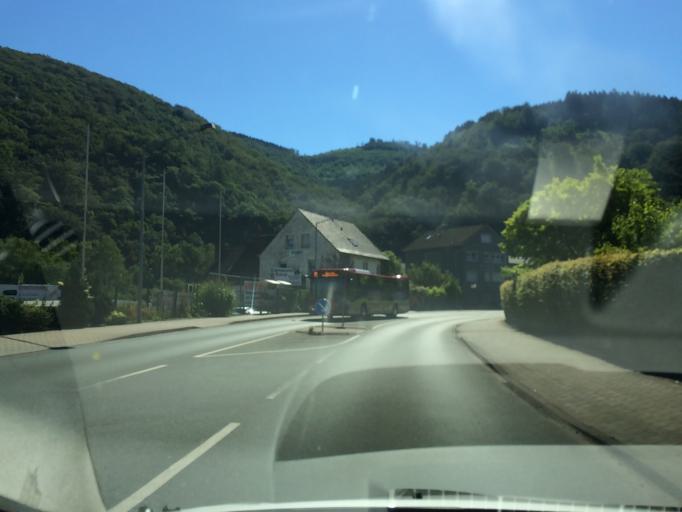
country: DE
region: North Rhine-Westphalia
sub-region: Regierungsbezirk Arnsberg
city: Nachrodt-Wiblingwerde
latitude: 51.3333
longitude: 7.6511
